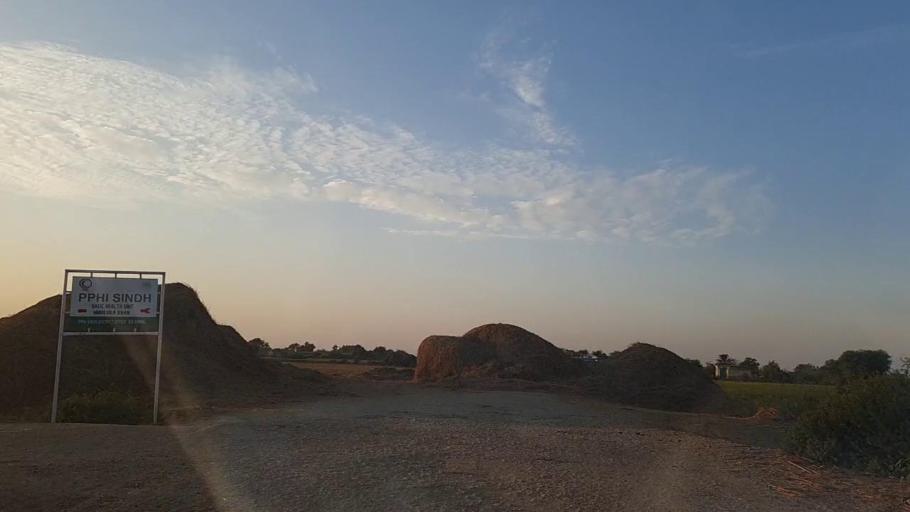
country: PK
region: Sindh
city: Chuhar Jamali
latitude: 24.4562
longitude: 68.1165
